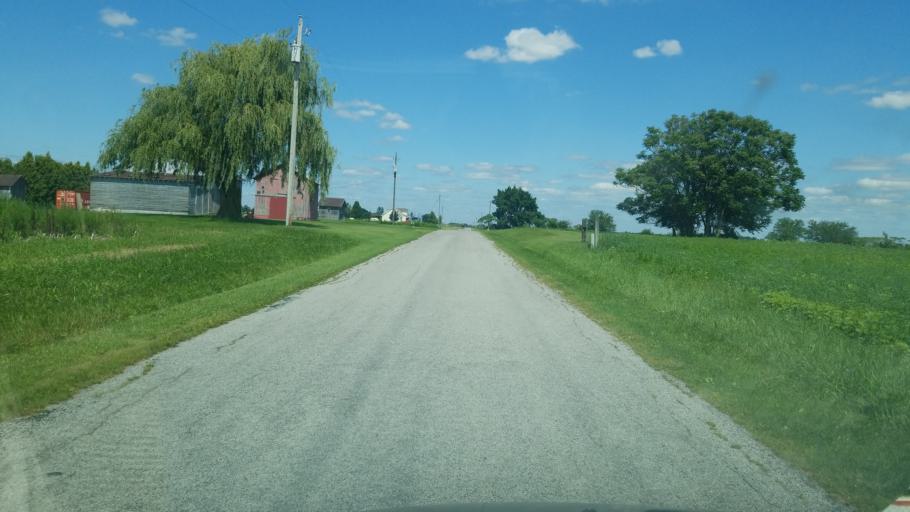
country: US
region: Ohio
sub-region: Fulton County
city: Delta
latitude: 41.6615
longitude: -84.0161
